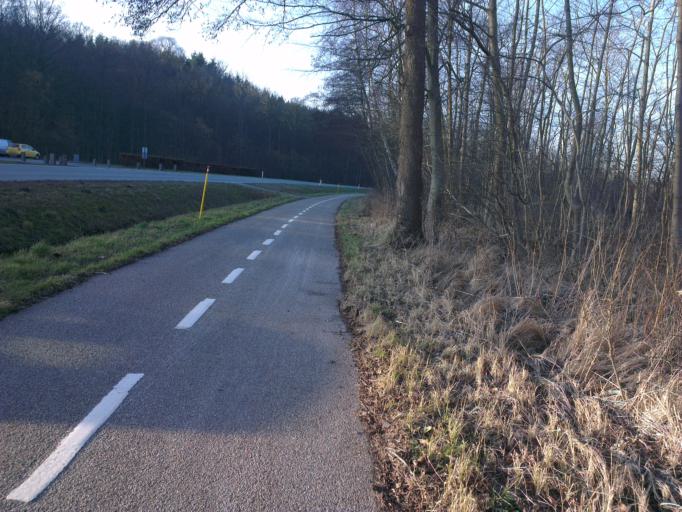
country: DK
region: Capital Region
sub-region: Frederikssund Kommune
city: Frederikssund
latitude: 55.8432
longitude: 12.0308
